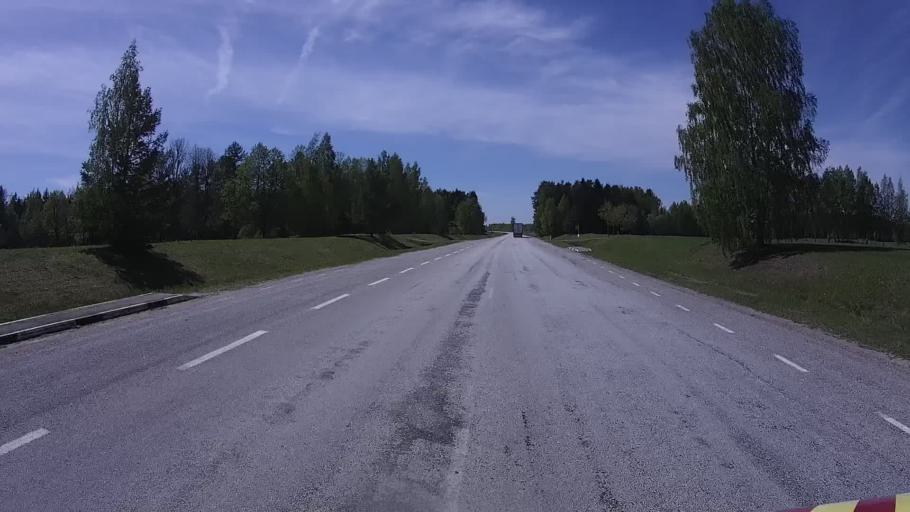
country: EE
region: Vorumaa
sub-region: Voru linn
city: Voru
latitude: 57.7512
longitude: 26.8227
